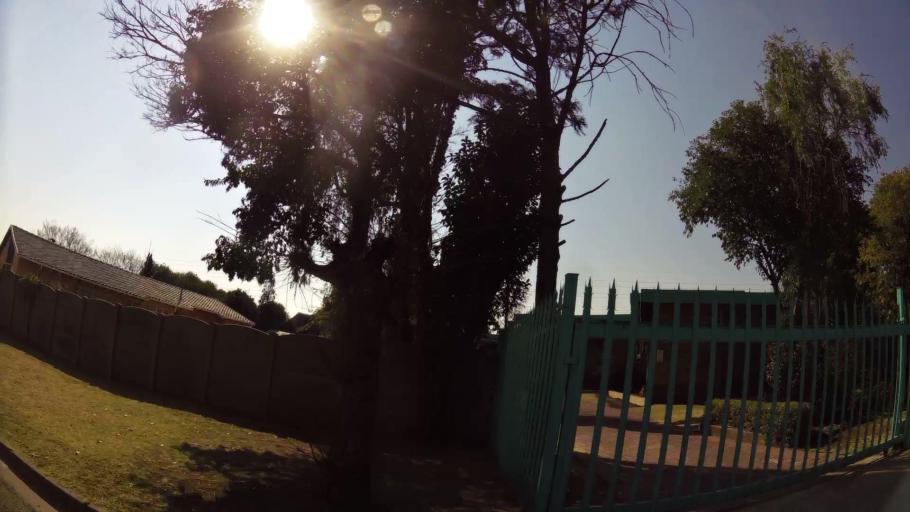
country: ZA
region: Gauteng
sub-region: Ekurhuleni Metropolitan Municipality
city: Boksburg
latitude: -26.2327
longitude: 28.2777
